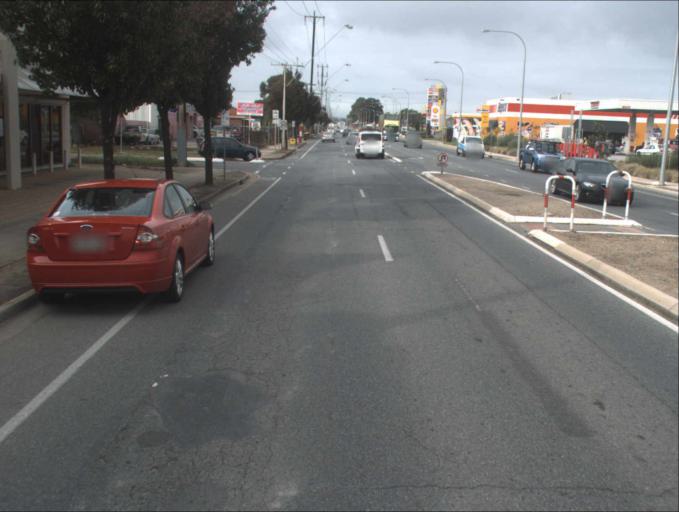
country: AU
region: South Australia
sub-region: Port Adelaide Enfield
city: Blair Athol
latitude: -34.8631
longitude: 138.5833
